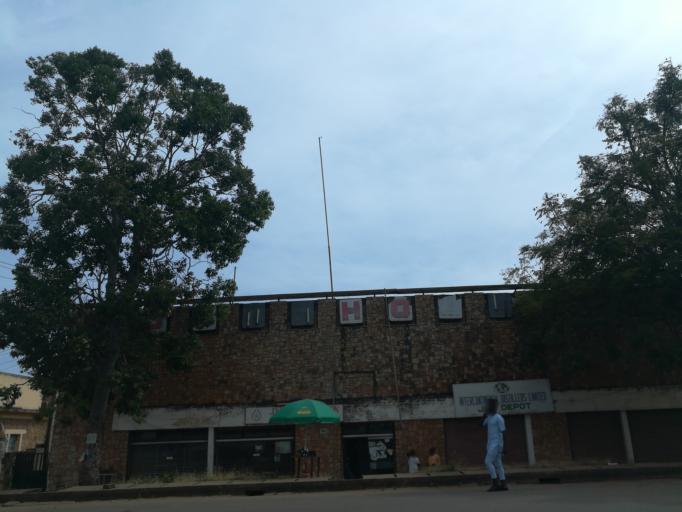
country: NG
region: Plateau
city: Jos
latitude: 9.9132
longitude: 8.8903
